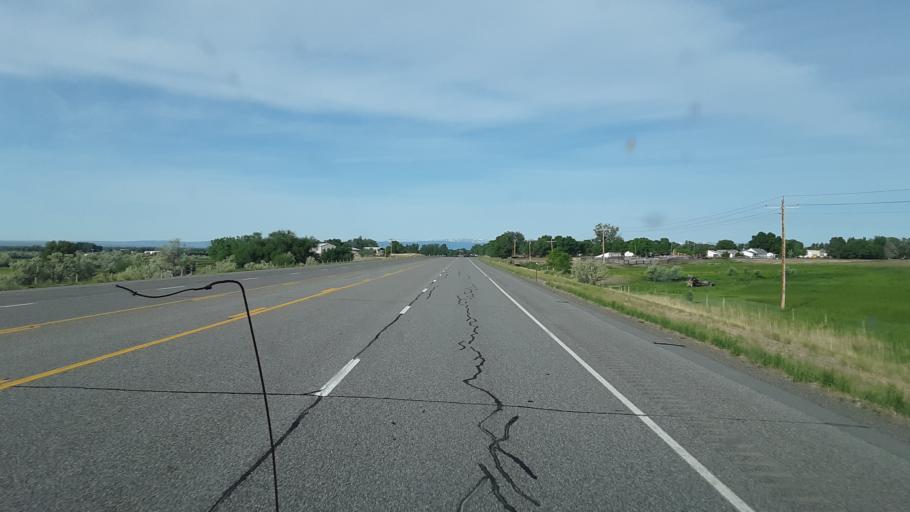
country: US
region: Wyoming
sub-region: Fremont County
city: Riverton
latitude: 43.1017
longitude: -108.3529
